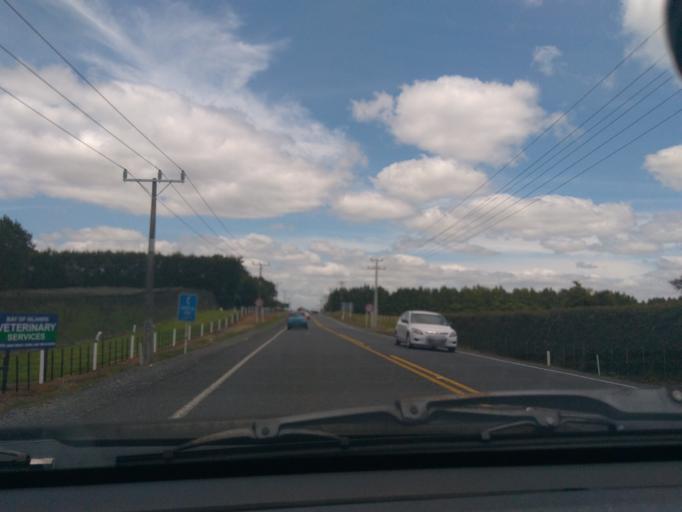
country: NZ
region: Northland
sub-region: Far North District
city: Kerikeri
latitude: -35.2033
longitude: 173.9138
